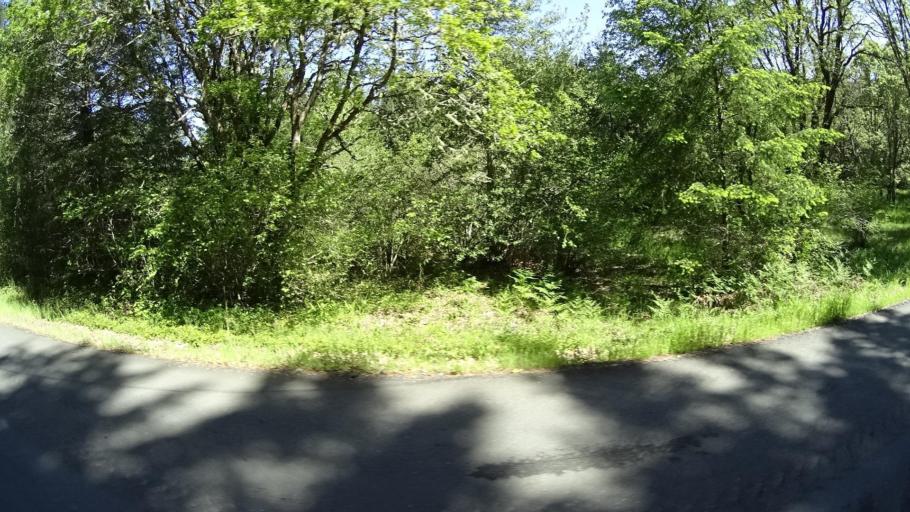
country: US
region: California
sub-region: Humboldt County
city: Rio Dell
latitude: 40.2489
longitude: -124.1748
